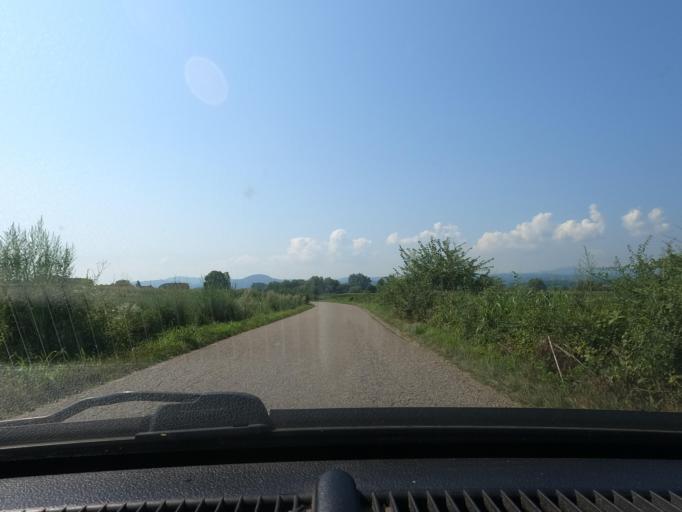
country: RS
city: Jarebice
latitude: 44.5388
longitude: 19.3710
